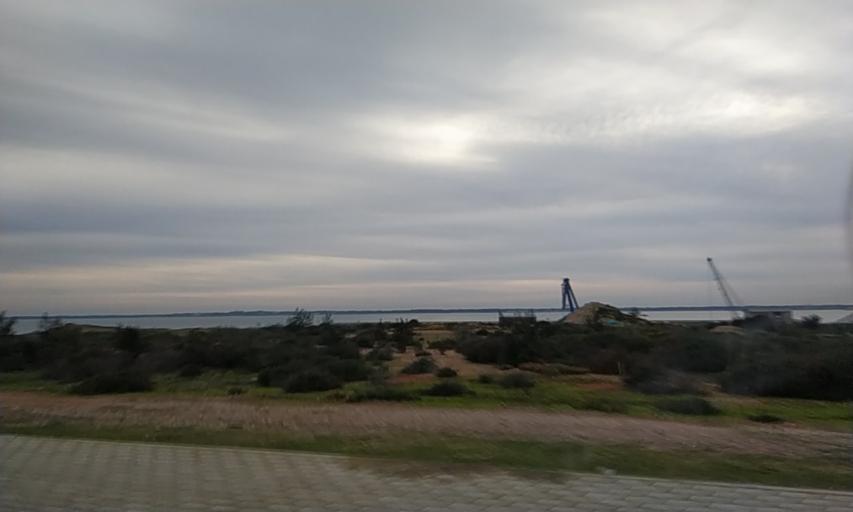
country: PT
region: Setubal
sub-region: Setubal
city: Setubal
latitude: 38.5026
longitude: -8.8388
